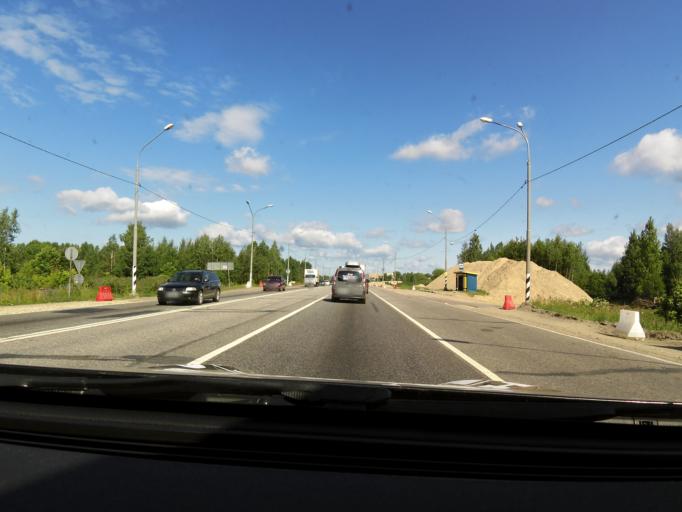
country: RU
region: Tverskaya
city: Tver
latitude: 56.8267
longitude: 35.8114
